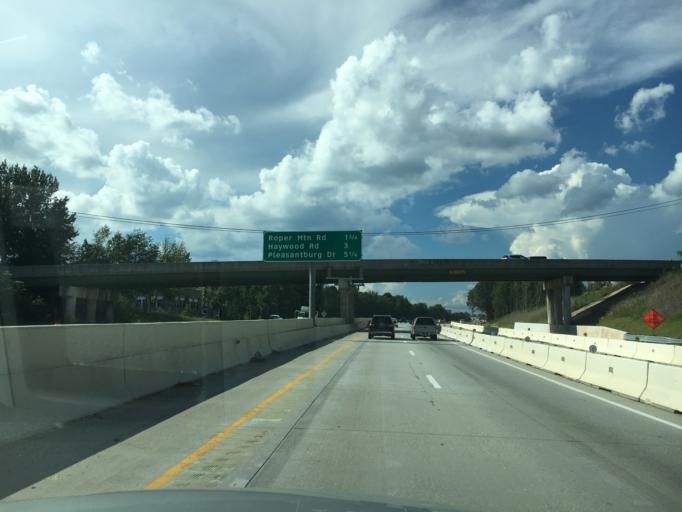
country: US
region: South Carolina
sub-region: Greenville County
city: Mauldin
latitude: 34.8143
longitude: -82.2890
